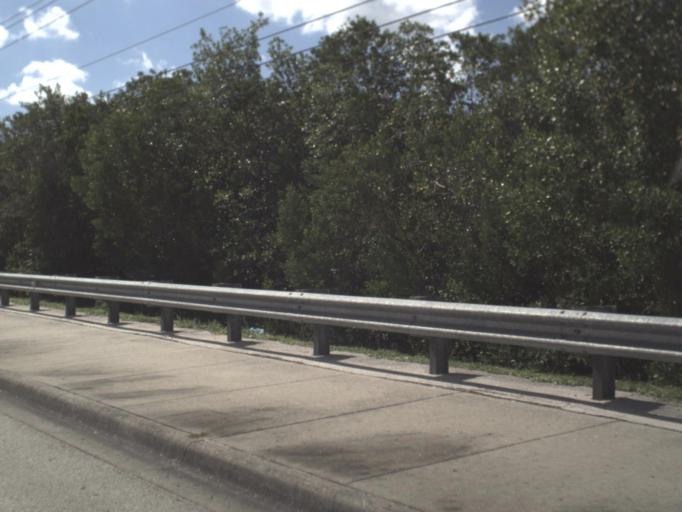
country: US
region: Florida
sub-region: Collier County
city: Naples Park
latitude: 26.2844
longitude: -81.8020
